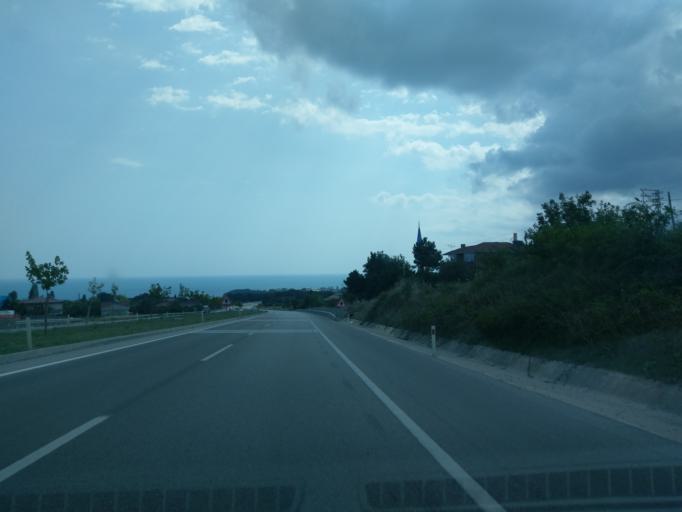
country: TR
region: Sinop
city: Kabali
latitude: 41.8481
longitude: 35.1288
